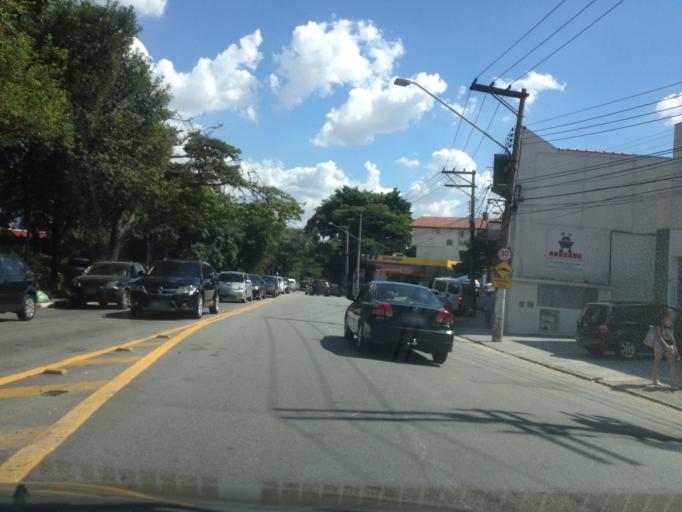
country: BR
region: Sao Paulo
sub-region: Sao Paulo
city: Sao Paulo
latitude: -23.5458
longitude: -46.7025
